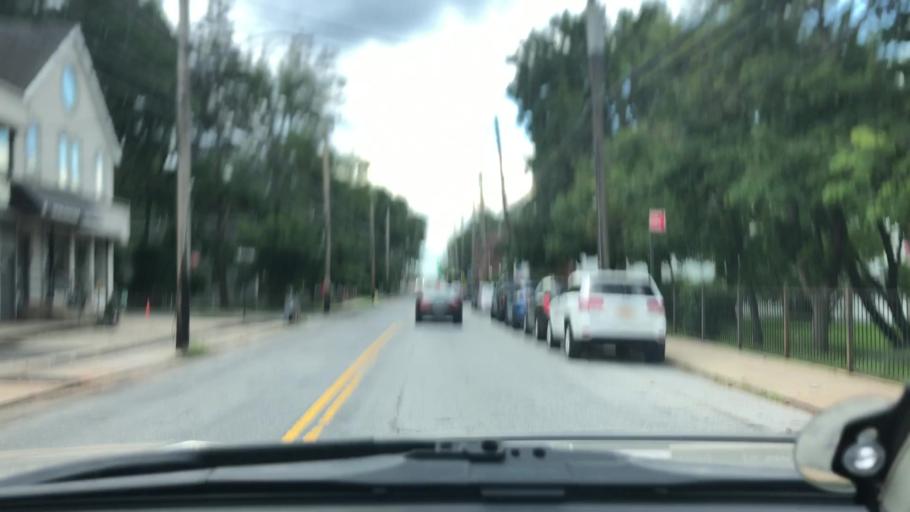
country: US
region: New York
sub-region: Richmond County
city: Bloomfield
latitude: 40.5931
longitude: -74.1884
